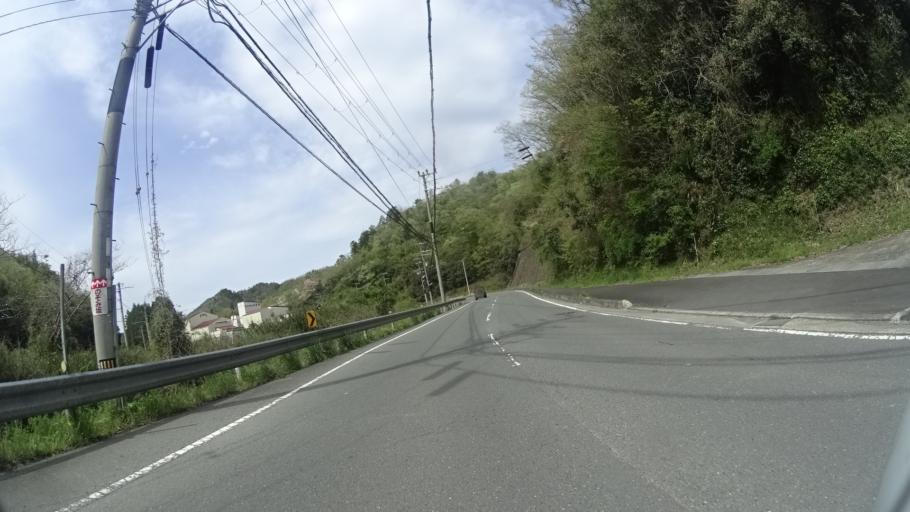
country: JP
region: Kyoto
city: Kameoka
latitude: 35.1687
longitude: 135.4974
